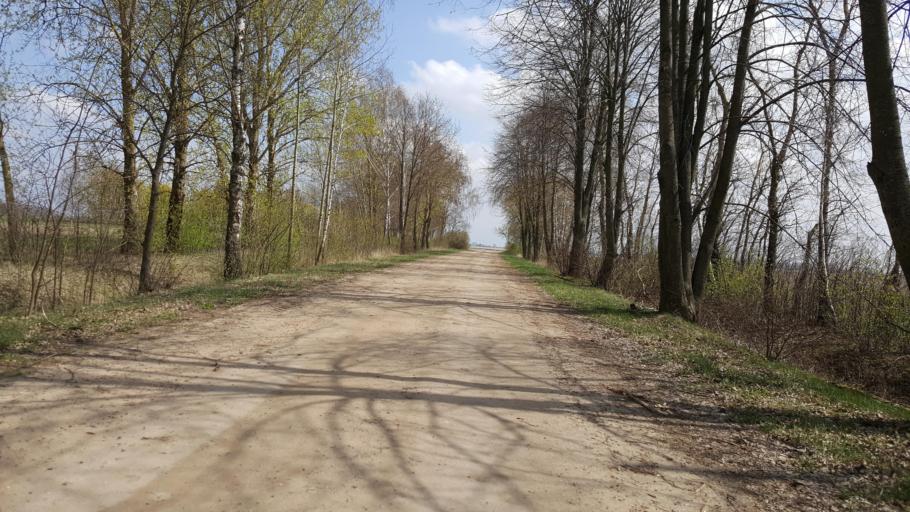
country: BY
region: Brest
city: Zhabinka
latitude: 52.2642
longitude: 24.0139
